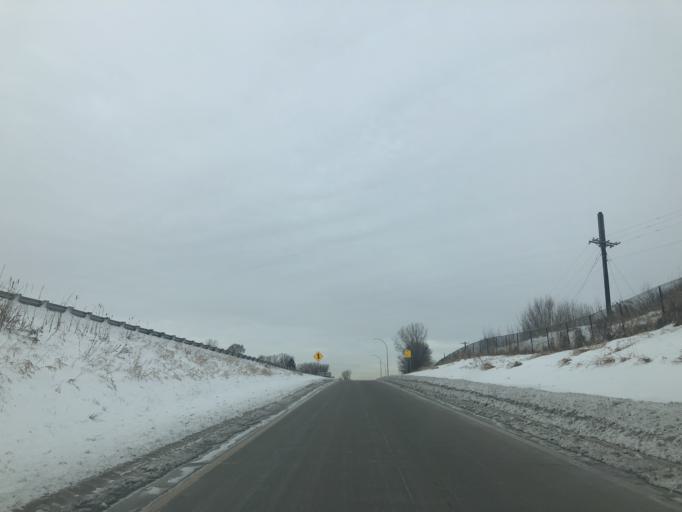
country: US
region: Minnesota
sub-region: Ramsey County
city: New Brighton
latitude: 45.0798
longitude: -93.1765
